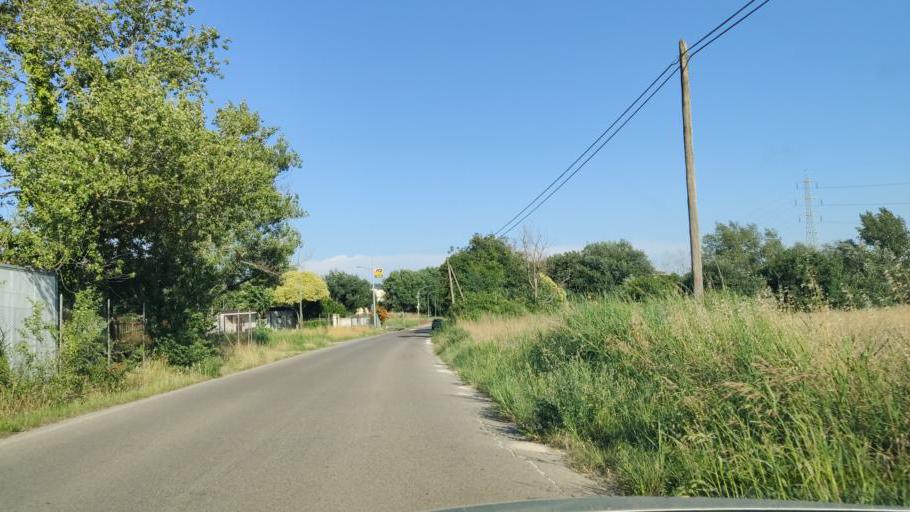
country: IT
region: Latium
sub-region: Provincia di Viterbo
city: Orte
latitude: 42.4684
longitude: 12.3887
